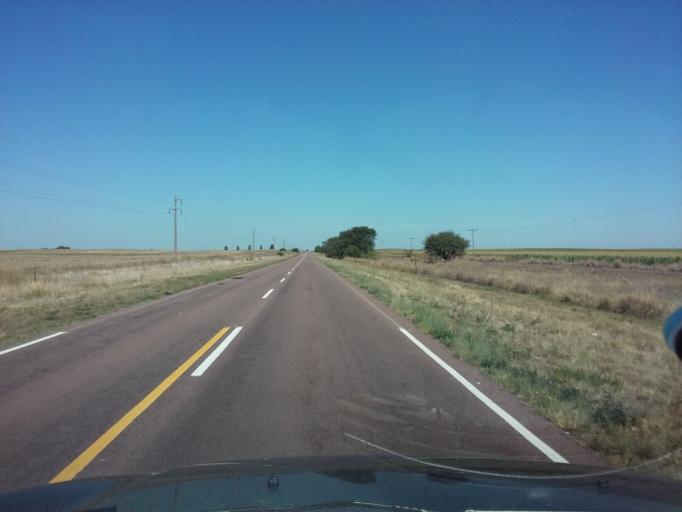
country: AR
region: La Pampa
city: Anguil
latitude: -36.4854
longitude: -63.9437
